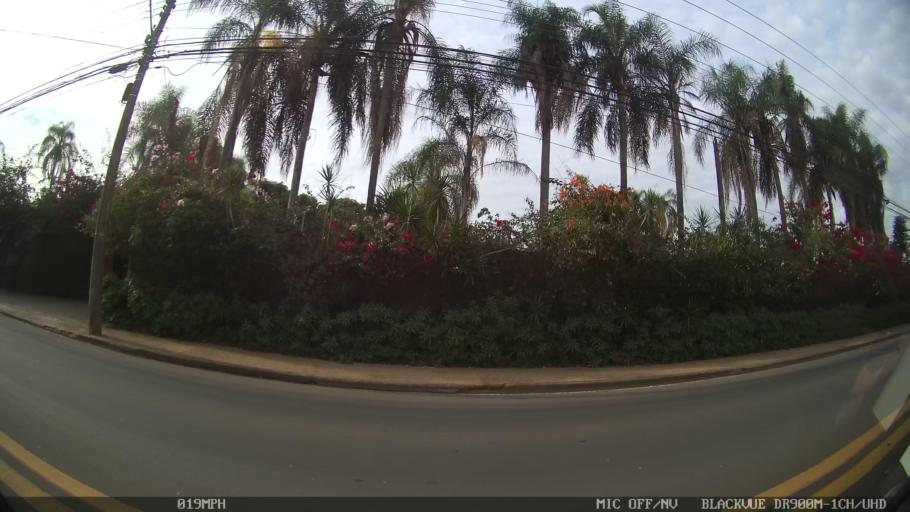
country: BR
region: Sao Paulo
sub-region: Piracicaba
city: Piracicaba
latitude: -22.7411
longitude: -47.6192
